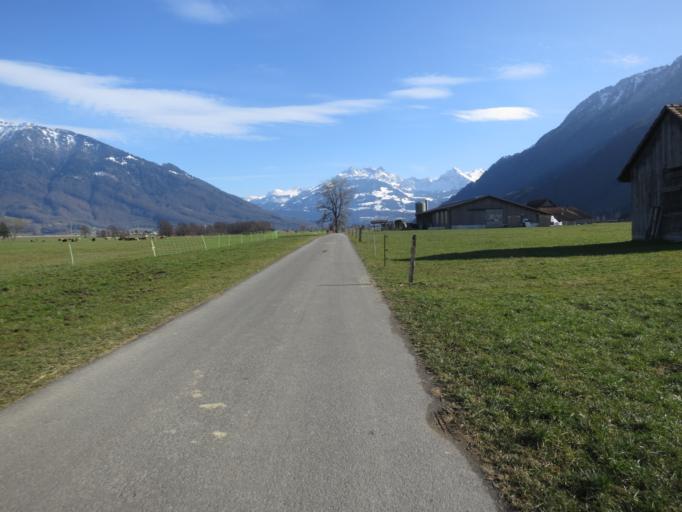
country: CH
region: Schwyz
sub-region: Bezirk March
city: Reichenburg
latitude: 47.1694
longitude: 8.9972
